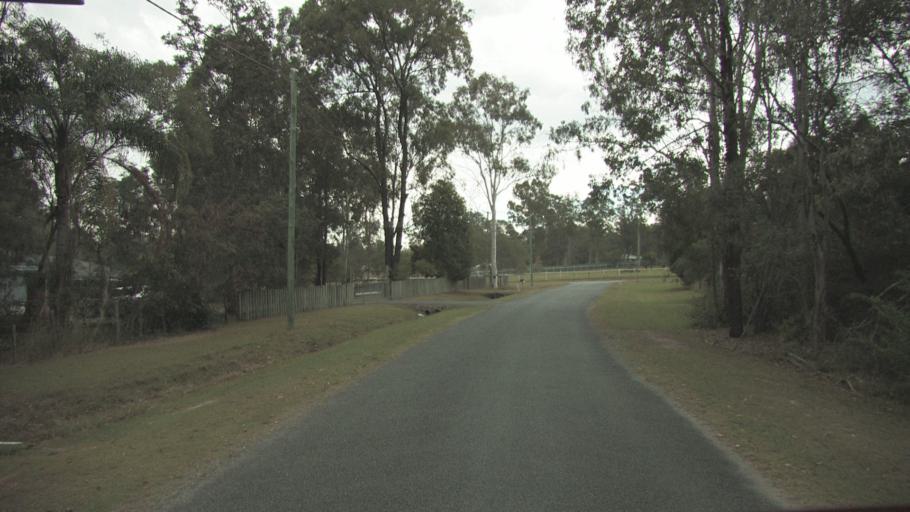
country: AU
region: Queensland
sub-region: Logan
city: Chambers Flat
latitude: -27.7886
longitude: 153.1161
